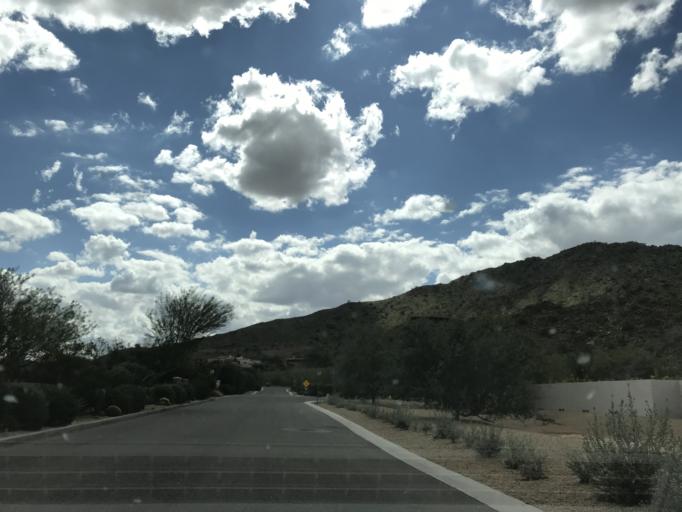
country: US
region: Arizona
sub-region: Maricopa County
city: Paradise Valley
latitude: 33.5196
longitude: -111.9497
